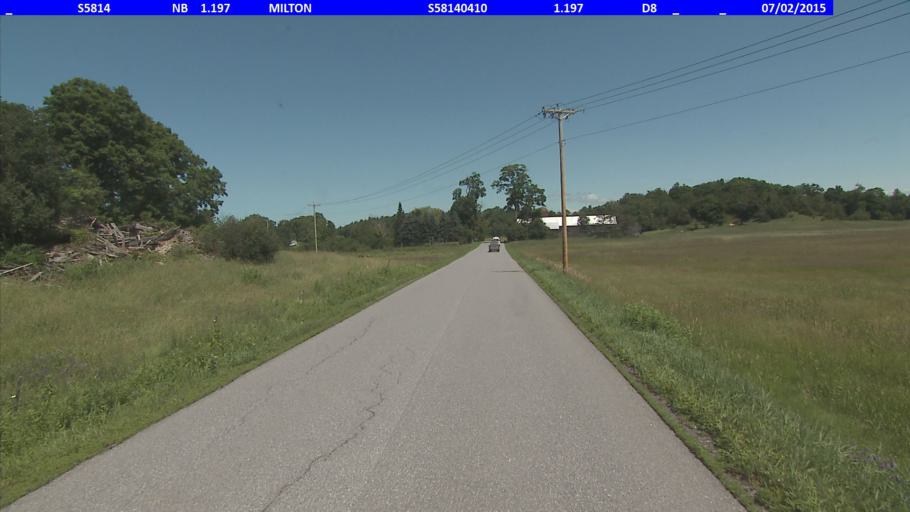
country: US
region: Vermont
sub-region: Chittenden County
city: Milton
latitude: 44.6452
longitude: -73.1672
